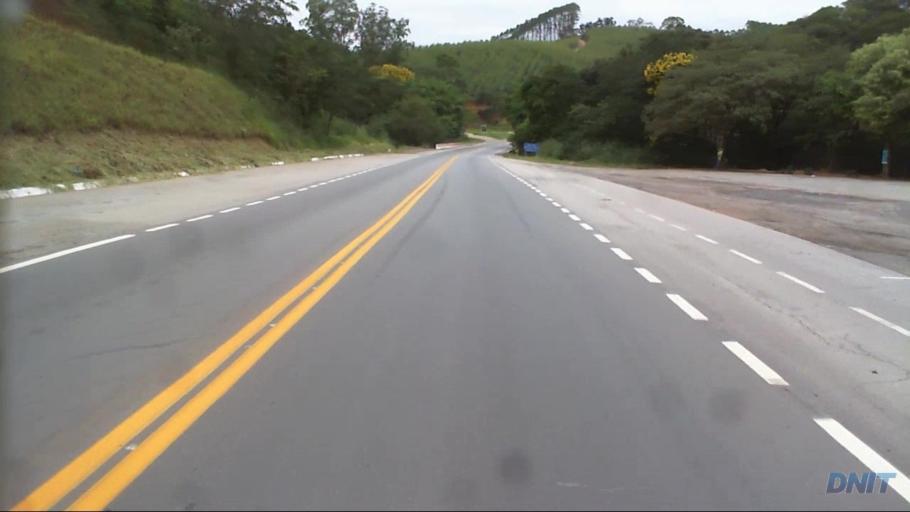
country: BR
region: Minas Gerais
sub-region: Joao Monlevade
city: Joao Monlevade
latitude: -19.8520
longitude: -43.2557
